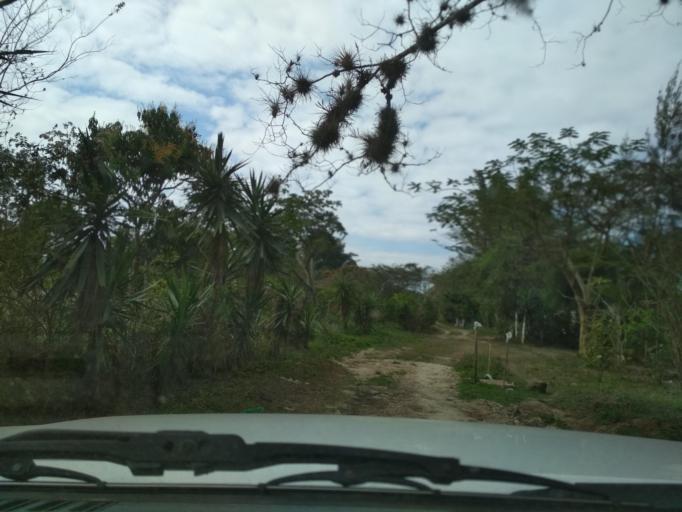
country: MX
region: Veracruz
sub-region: Coatepec
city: Tuzamapan
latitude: 19.3679
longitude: -96.8787
